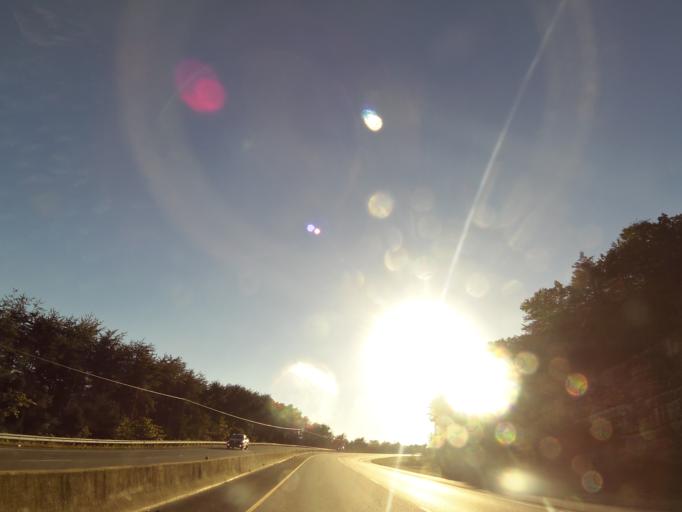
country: US
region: Tennessee
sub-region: Grainger County
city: Bean Station
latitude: 36.3531
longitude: -83.3813
